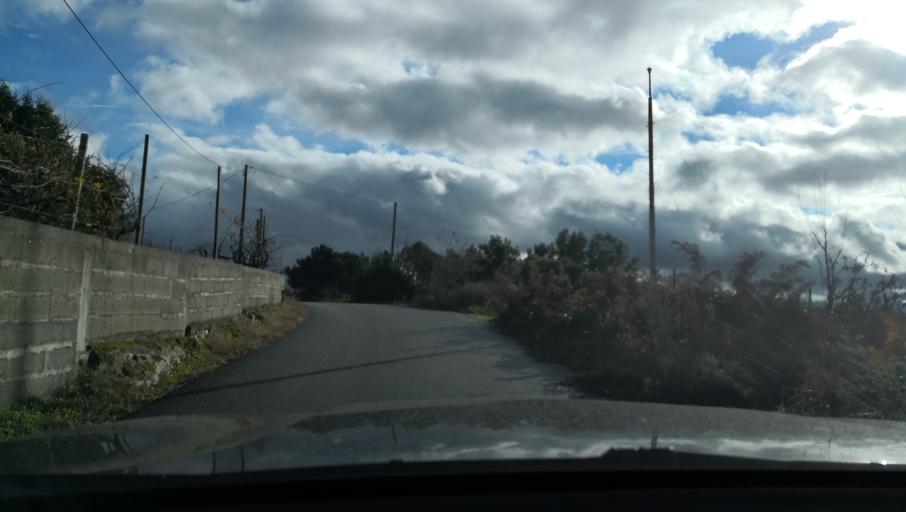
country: PT
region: Vila Real
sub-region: Vila Real
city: Vila Real
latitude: 41.2684
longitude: -7.7237
